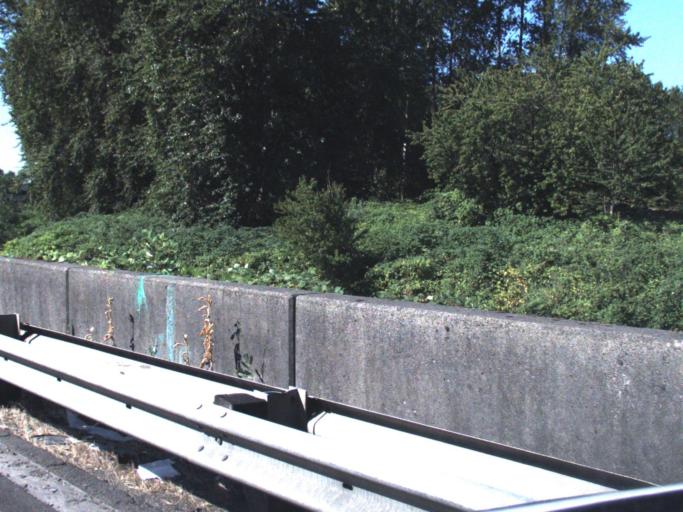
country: US
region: Washington
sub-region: King County
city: Tukwila
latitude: 47.4485
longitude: -122.2433
